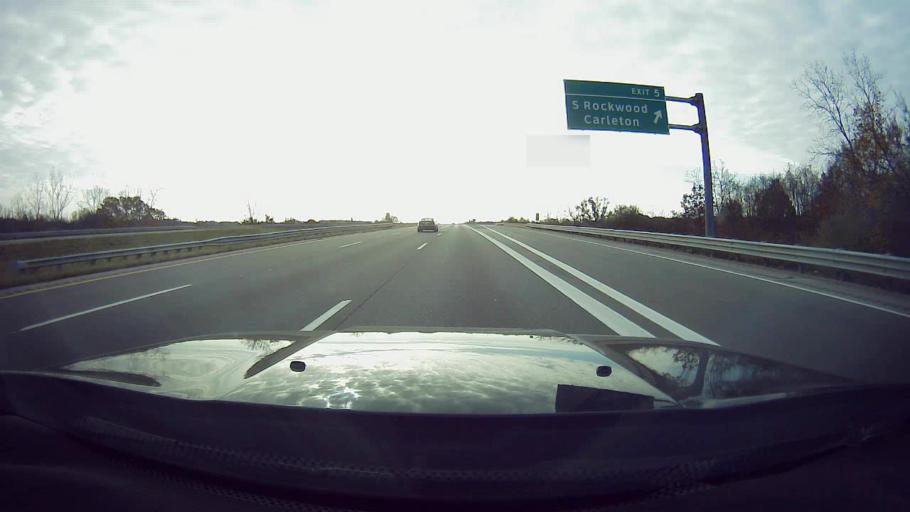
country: US
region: Michigan
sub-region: Monroe County
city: Carleton
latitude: 42.0708
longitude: -83.3662
